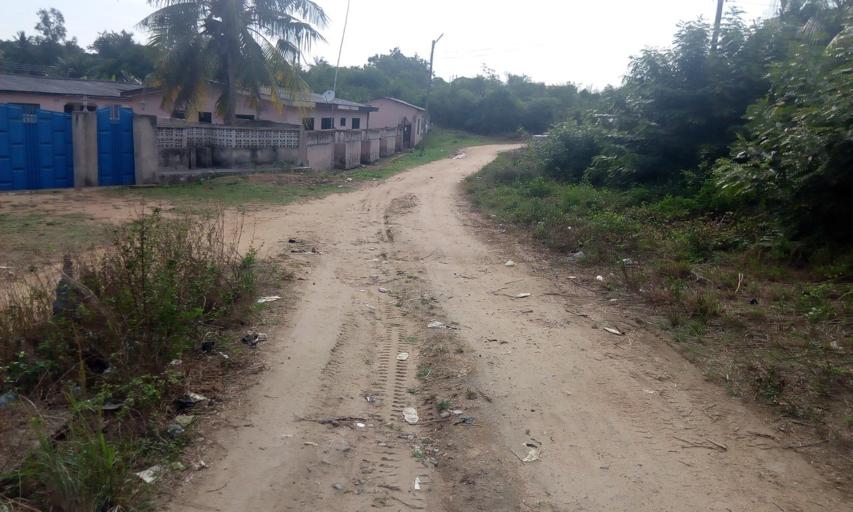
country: GH
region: Central
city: Winneba
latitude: 5.3599
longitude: -0.6244
